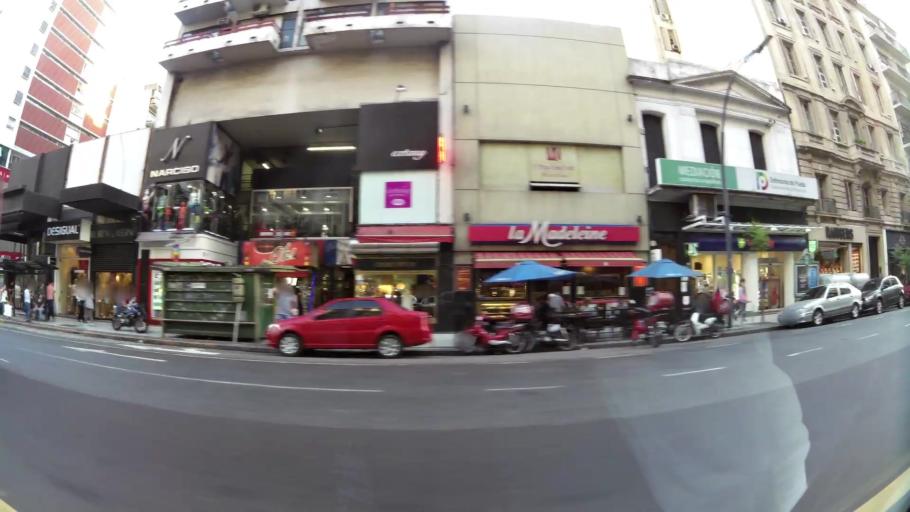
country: AR
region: Buenos Aires F.D.
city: Retiro
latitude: -34.5961
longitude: -58.3924
